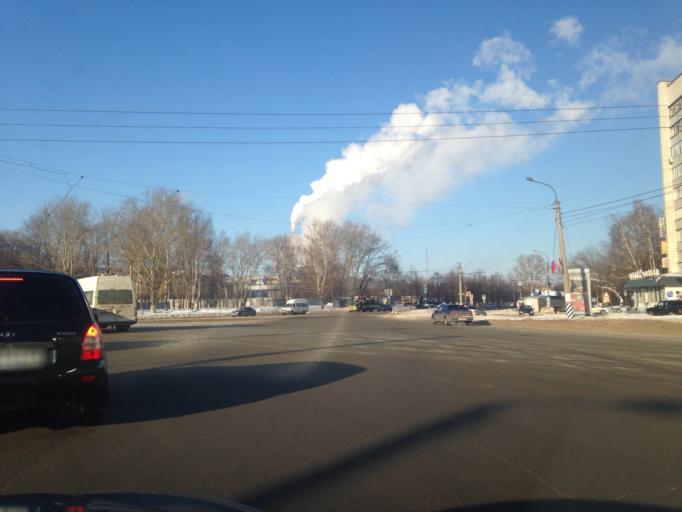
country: RU
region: Ulyanovsk
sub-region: Ulyanovskiy Rayon
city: Ulyanovsk
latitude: 54.3066
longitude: 48.3504
